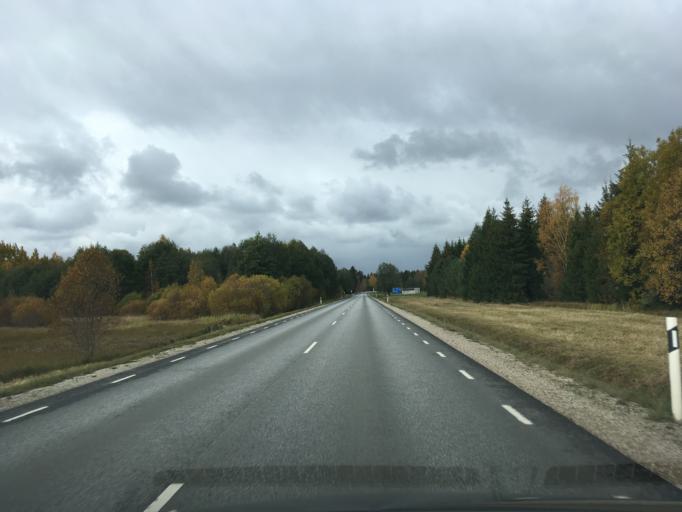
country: EE
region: Harju
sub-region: Anija vald
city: Kehra
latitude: 59.3085
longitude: 25.3518
